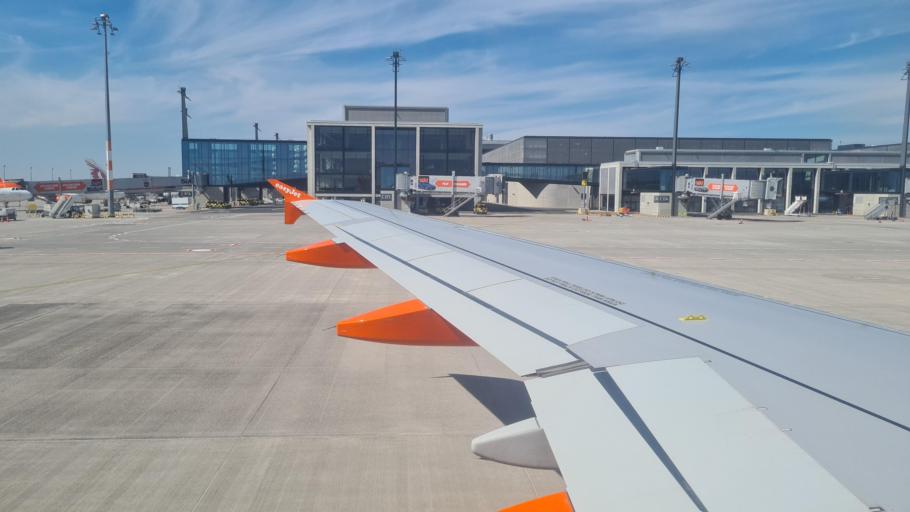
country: DE
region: Brandenburg
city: Schonefeld
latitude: 52.3596
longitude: 13.5100
